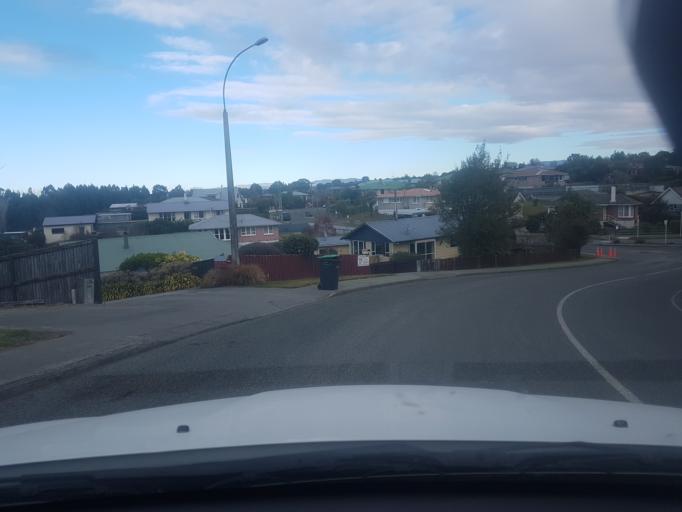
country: NZ
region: Canterbury
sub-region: Timaru District
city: Timaru
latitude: -44.3925
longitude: 171.2194
